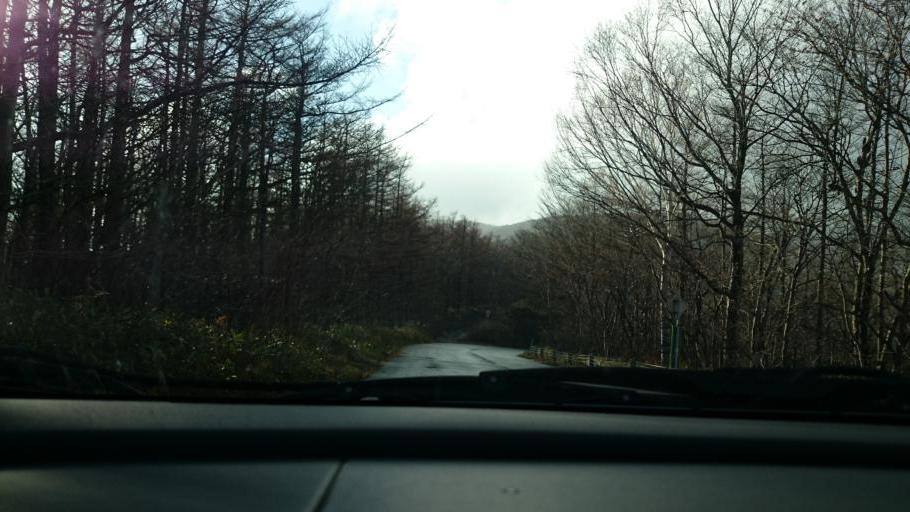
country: JP
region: Tochigi
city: Kuroiso
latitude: 37.1379
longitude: 140.0178
